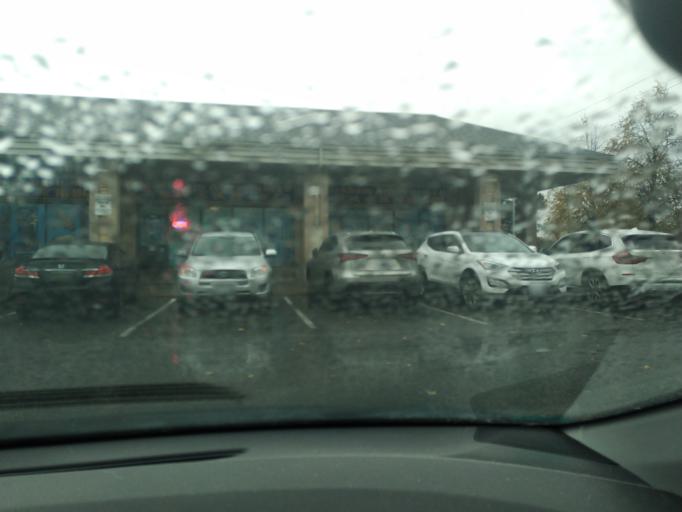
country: CA
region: Ontario
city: Markham
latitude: 43.8303
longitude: -79.2801
